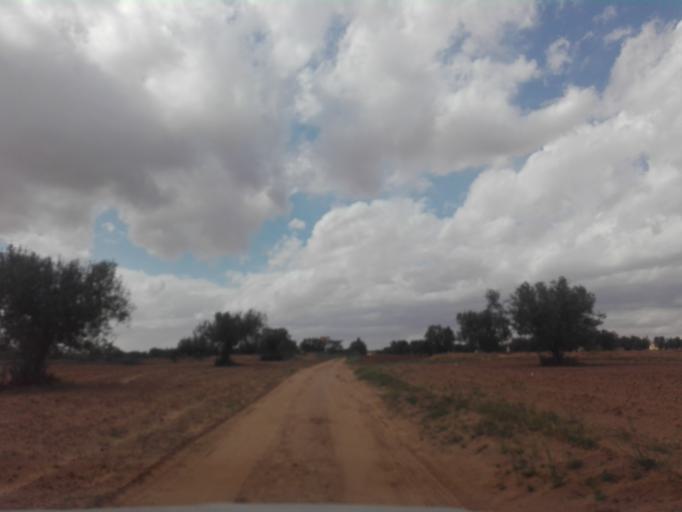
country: TN
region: Safaqis
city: Sfax
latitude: 34.6937
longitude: 10.4479
